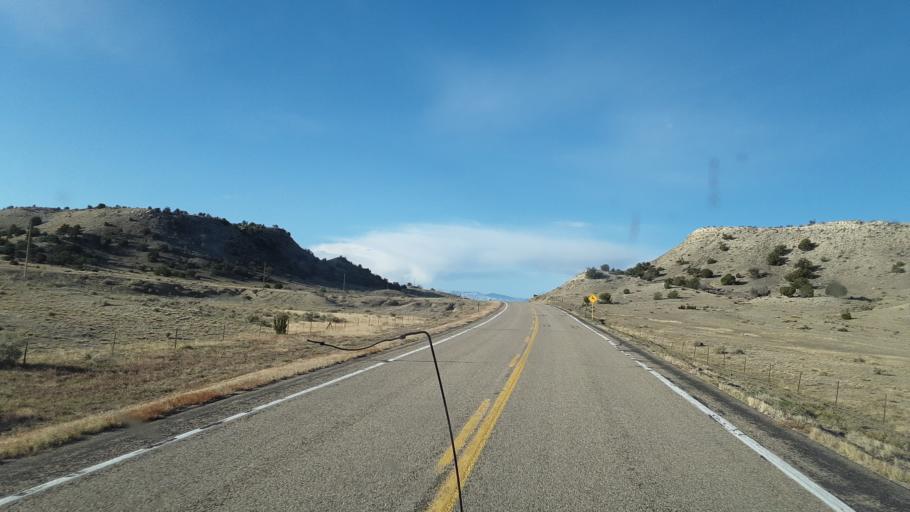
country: US
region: Colorado
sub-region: Huerfano County
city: Walsenburg
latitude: 37.6936
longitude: -104.6287
